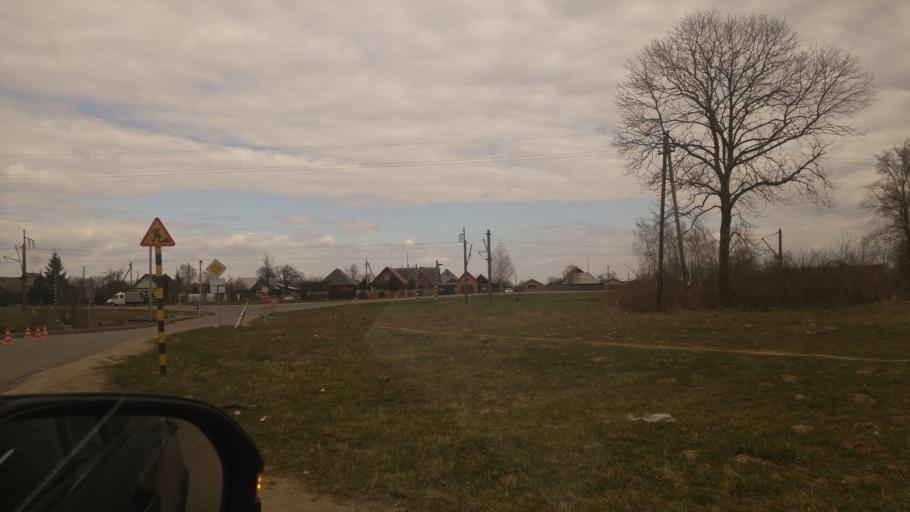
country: BY
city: Michanovichi
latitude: 53.6715
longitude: 27.7489
